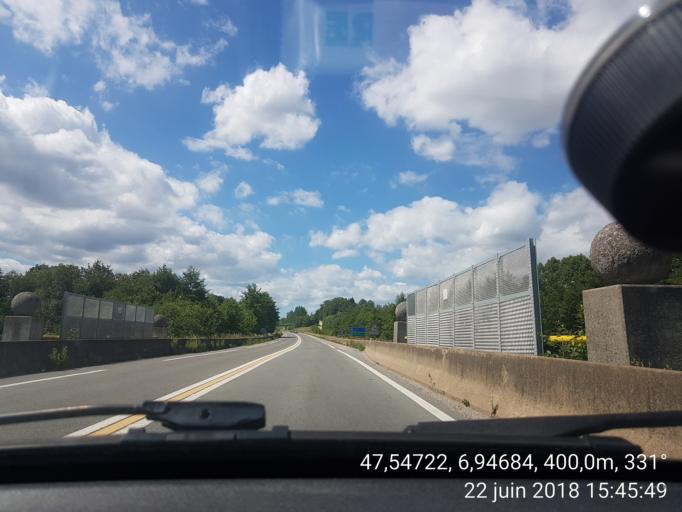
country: FR
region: Franche-Comte
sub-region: Territoire de Belfort
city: Morvillars
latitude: 47.5470
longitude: 6.9470
